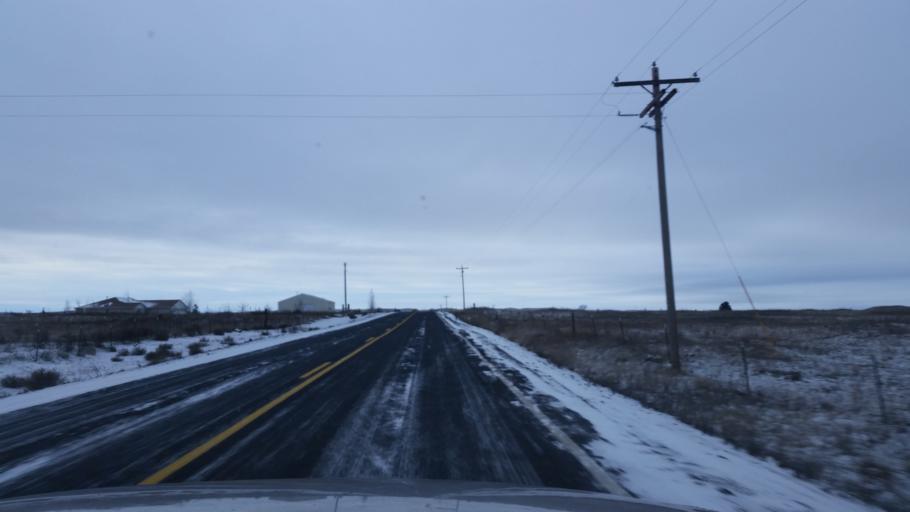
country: US
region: Washington
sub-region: Spokane County
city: Cheney
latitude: 47.4030
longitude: -117.4885
